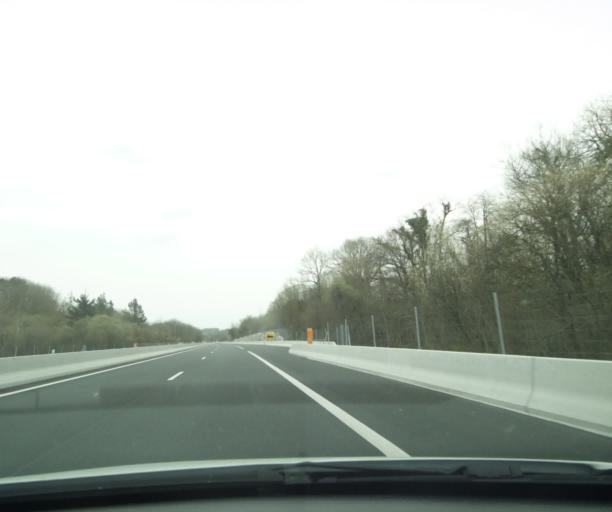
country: FR
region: Aquitaine
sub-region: Departement des Pyrenees-Atlantiques
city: Mouguerre
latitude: 43.4533
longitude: -1.3933
